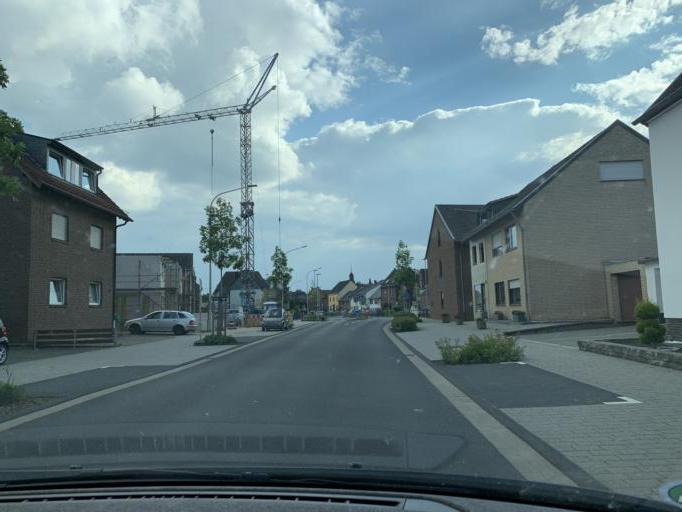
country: DE
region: North Rhine-Westphalia
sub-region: Regierungsbezirk Koln
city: Weilerswist
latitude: 50.7612
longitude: 6.8432
